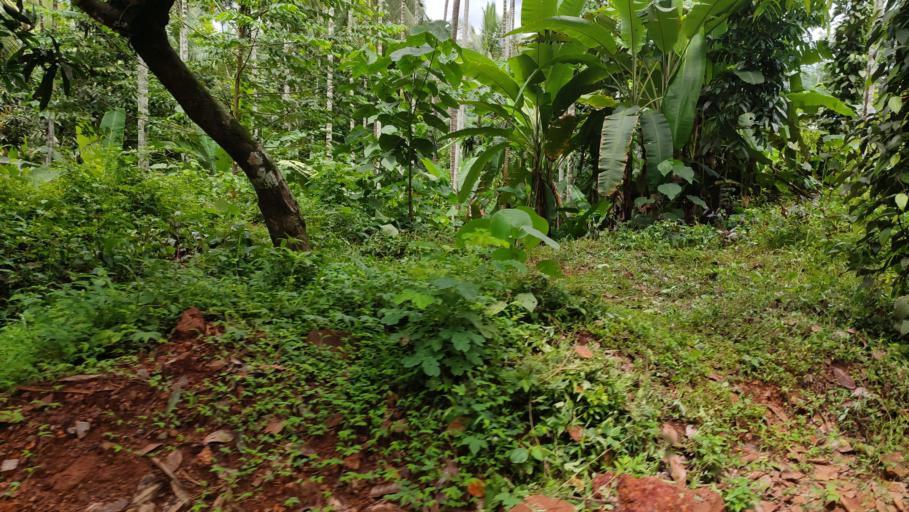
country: IN
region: Kerala
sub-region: Kasaragod District
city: Nileshwar
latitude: 12.2888
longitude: 75.2712
